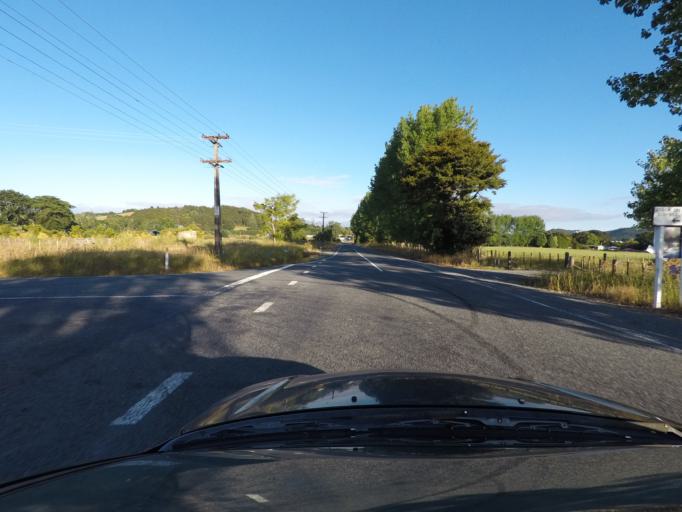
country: NZ
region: Northland
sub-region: Whangarei
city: Whangarei
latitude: -35.6443
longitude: 174.3013
